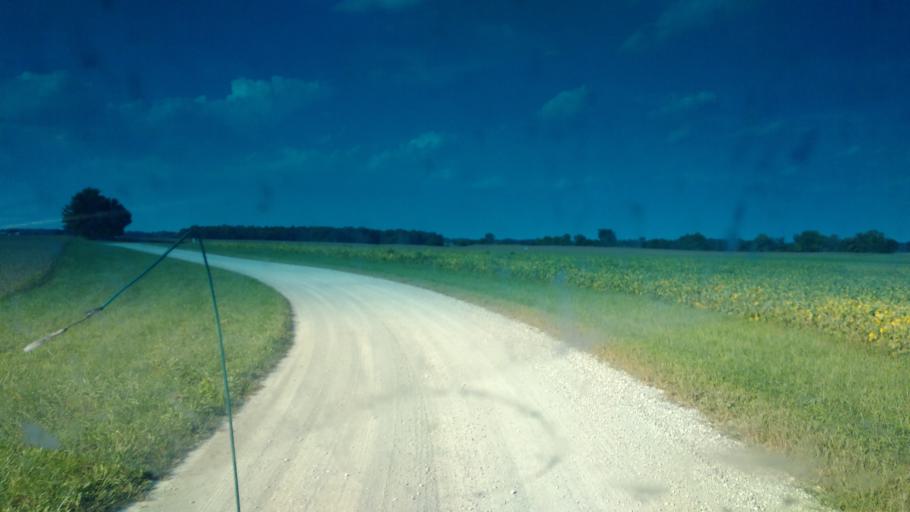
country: US
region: Ohio
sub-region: Wyandot County
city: Upper Sandusky
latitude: 40.9277
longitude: -83.2813
